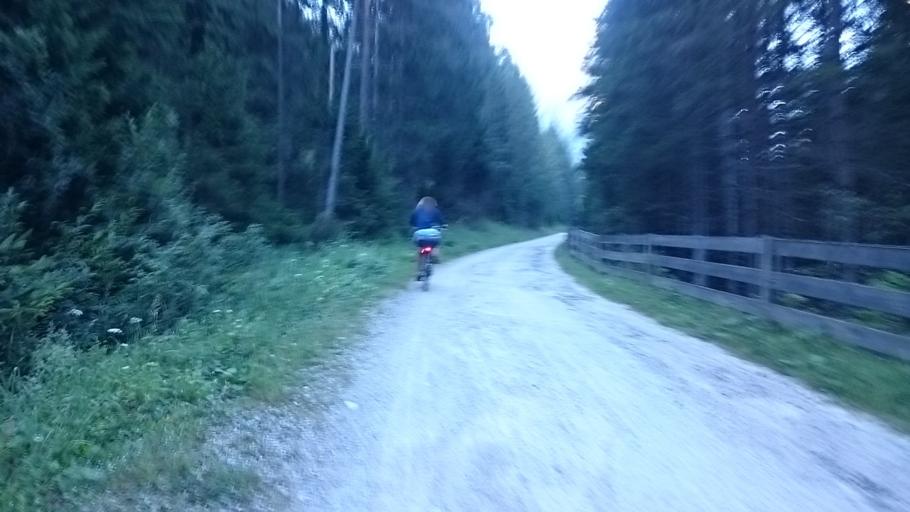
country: IT
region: Trentino-Alto Adige
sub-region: Bolzano
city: Dobbiaco
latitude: 46.6965
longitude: 12.2217
